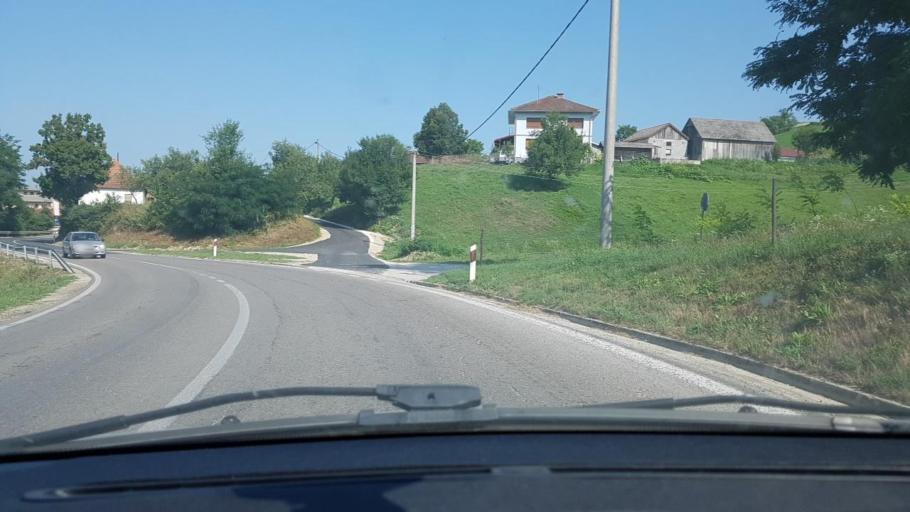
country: BA
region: Federation of Bosnia and Herzegovina
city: Mala Kladusa
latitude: 45.1302
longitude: 15.8659
